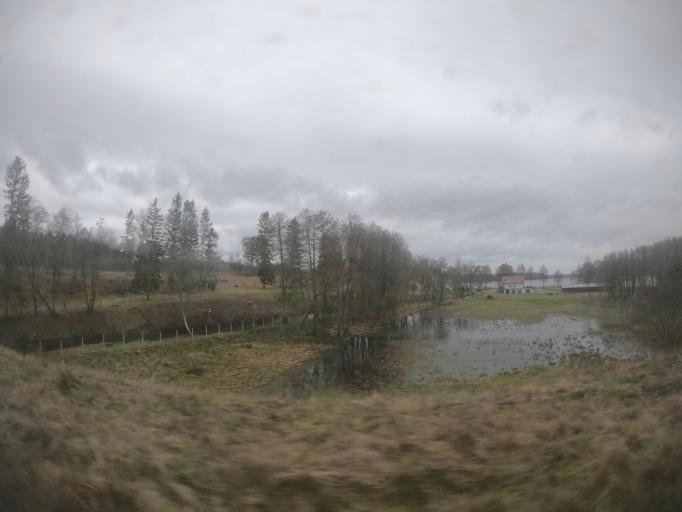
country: PL
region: West Pomeranian Voivodeship
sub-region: Powiat szczecinecki
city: Bialy Bor
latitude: 53.8322
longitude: 16.8749
